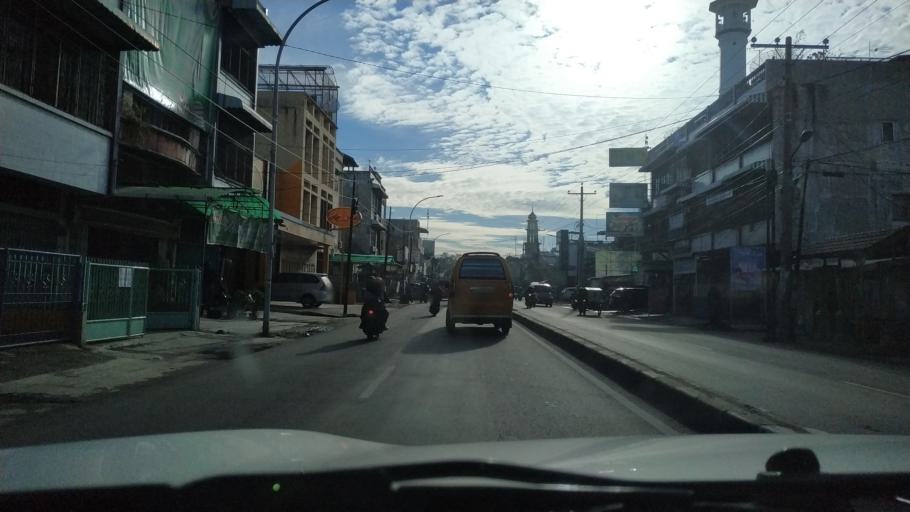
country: ID
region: North Sumatra
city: Medan
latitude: 3.5983
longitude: 98.6997
